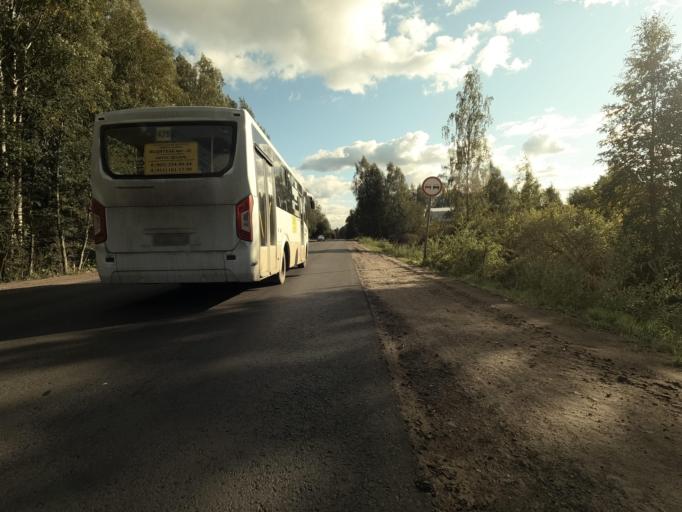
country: RU
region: Leningrad
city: Koltushi
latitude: 59.9288
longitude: 30.6641
